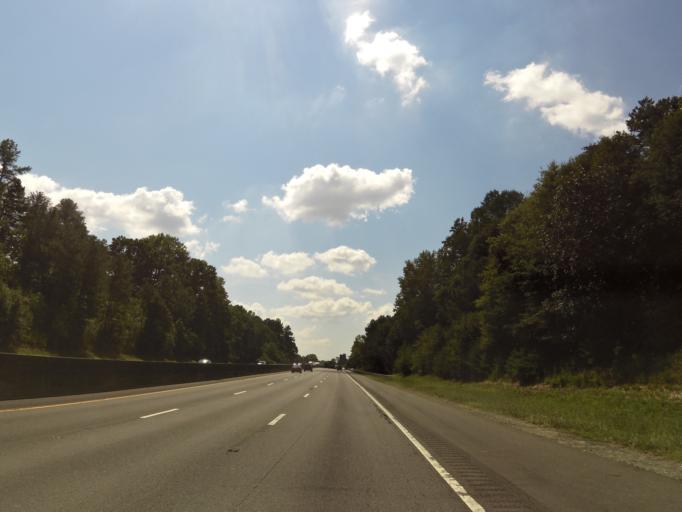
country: US
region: North Carolina
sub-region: Gaston County
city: Gastonia
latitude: 35.2838
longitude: -81.1770
